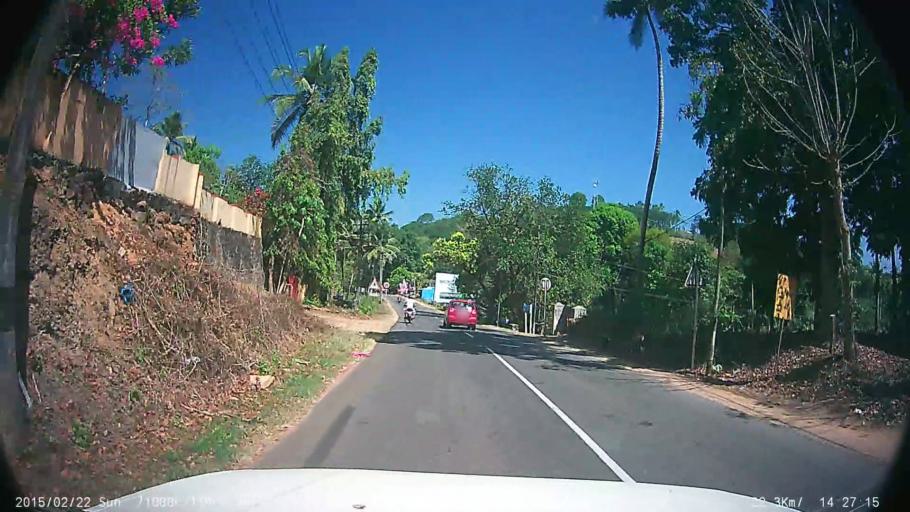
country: IN
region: Kerala
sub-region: Kottayam
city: Erattupetta
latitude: 9.5637
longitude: 76.7331
